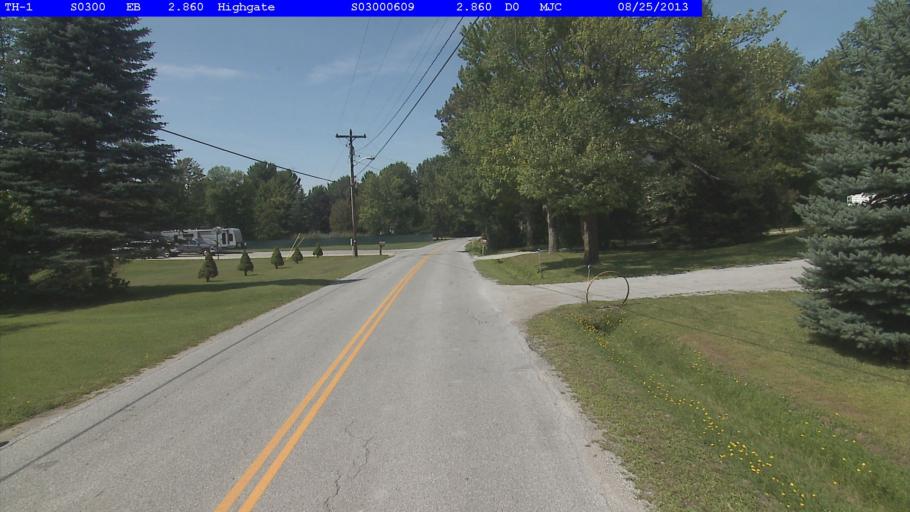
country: US
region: Vermont
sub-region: Franklin County
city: Swanton
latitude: 44.9633
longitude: -73.0979
